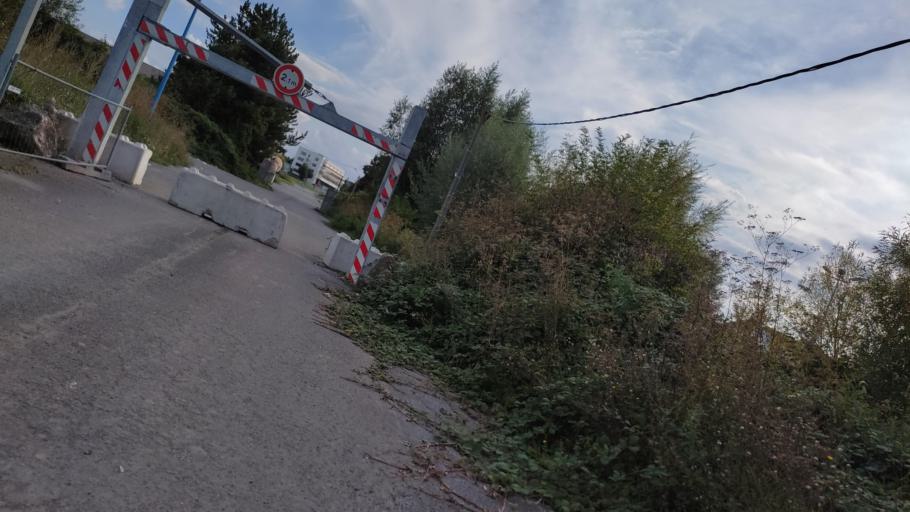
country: FR
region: Nord-Pas-de-Calais
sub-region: Departement du Pas-de-Calais
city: Arras
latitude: 50.2980
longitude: 2.7911
